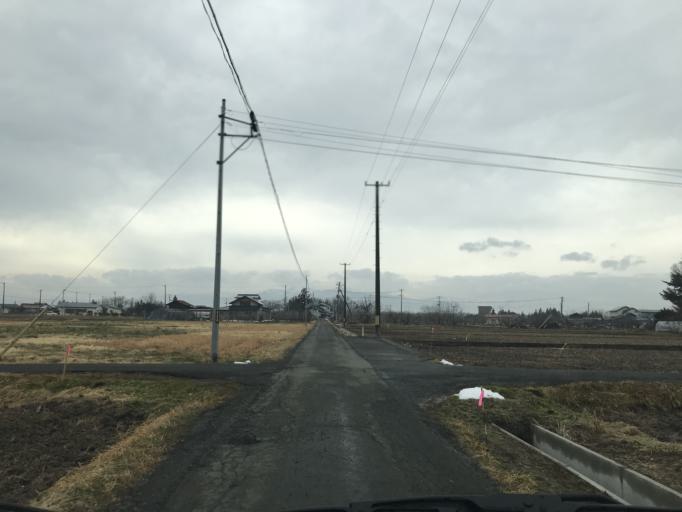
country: JP
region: Iwate
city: Mizusawa
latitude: 39.1836
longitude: 141.1333
